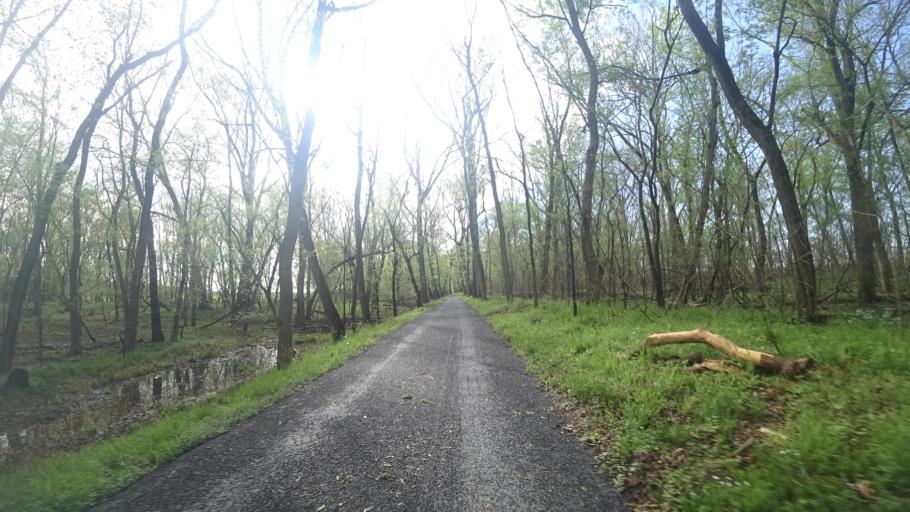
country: US
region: Virginia
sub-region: Loudoun County
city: University Center
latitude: 39.0859
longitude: -77.4579
